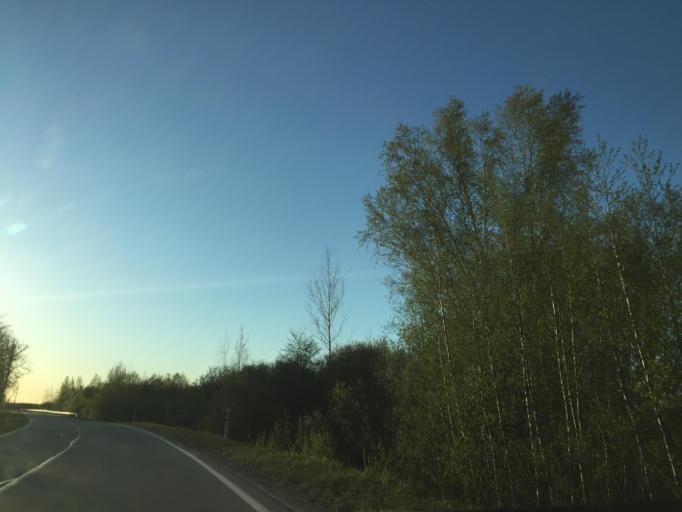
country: LV
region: Malpils
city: Malpils
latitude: 56.9048
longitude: 25.1040
